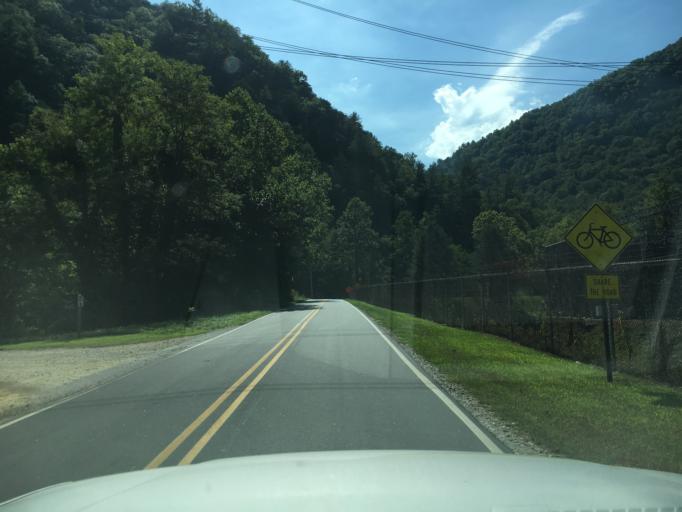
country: US
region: North Carolina
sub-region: Graham County
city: Robbinsville
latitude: 35.2725
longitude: -83.6767
